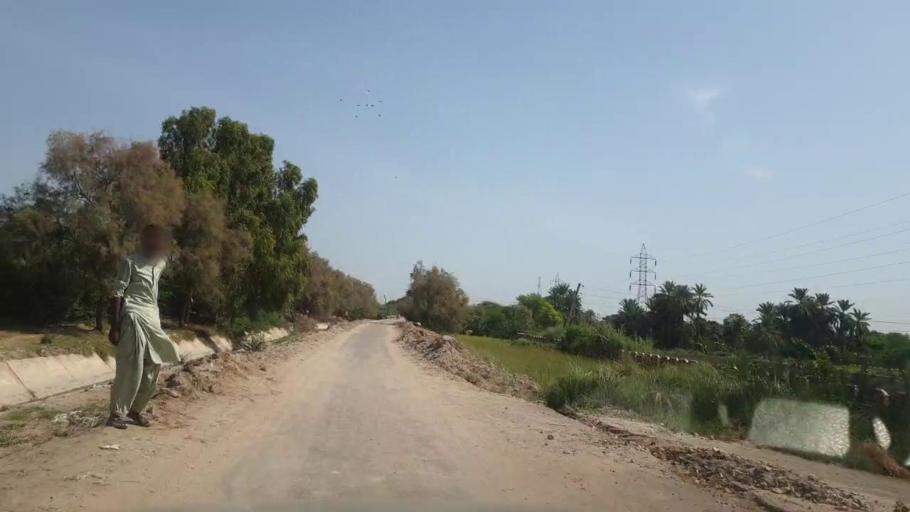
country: PK
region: Sindh
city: Rohri
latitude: 27.6714
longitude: 68.8820
